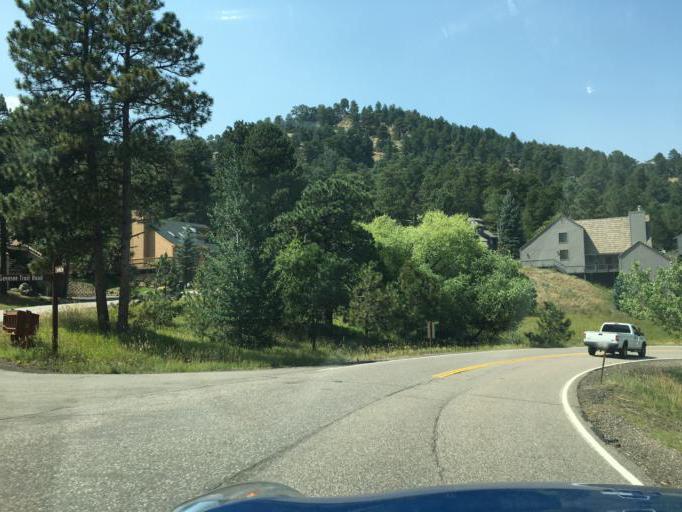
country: US
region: Colorado
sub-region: Jefferson County
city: Genesee
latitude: 39.6971
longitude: -105.2706
